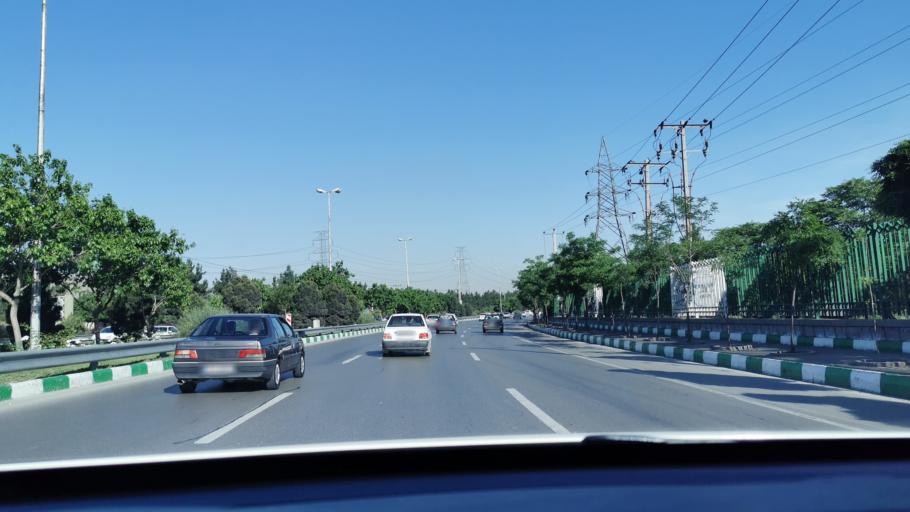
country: IR
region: Razavi Khorasan
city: Mashhad
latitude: 36.2575
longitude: 59.5903
